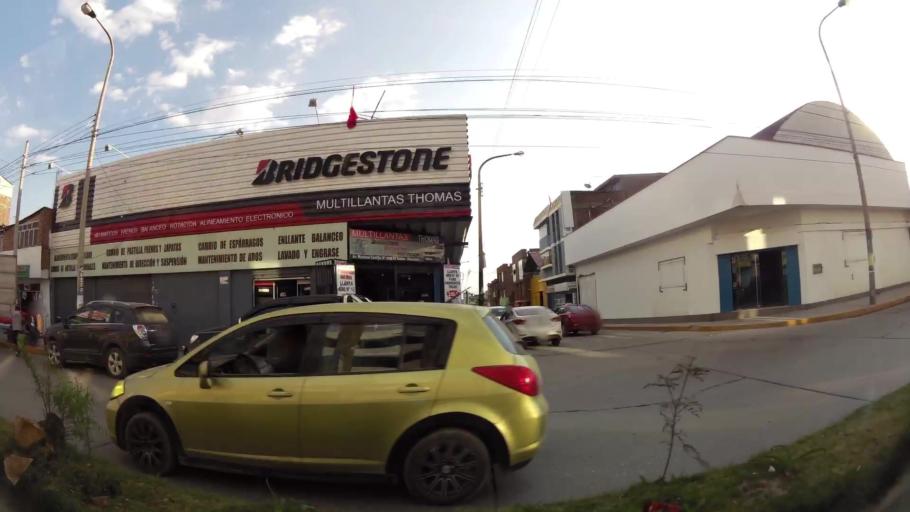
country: PE
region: Junin
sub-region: Provincia de Huancayo
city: El Tambo
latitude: -12.0525
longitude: -75.2203
